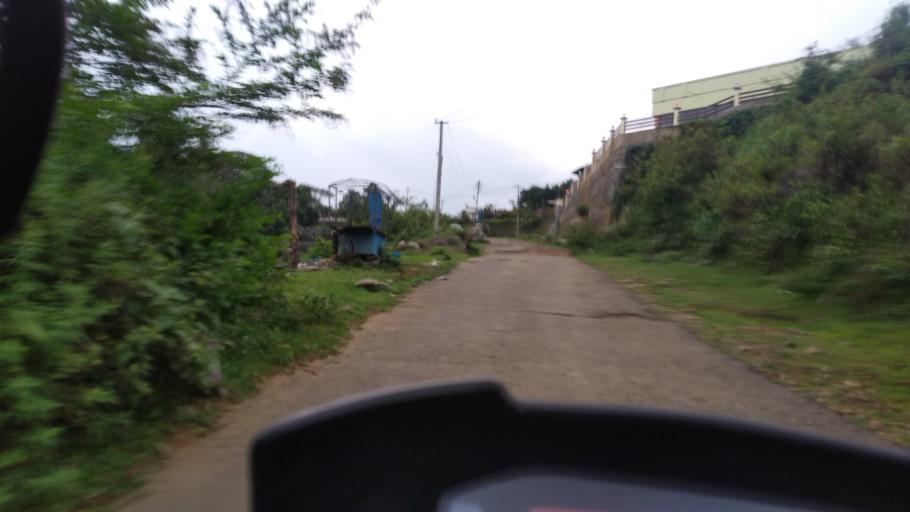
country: IN
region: Tamil Nadu
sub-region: Theni
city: Gudalur
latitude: 9.5469
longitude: 77.0356
